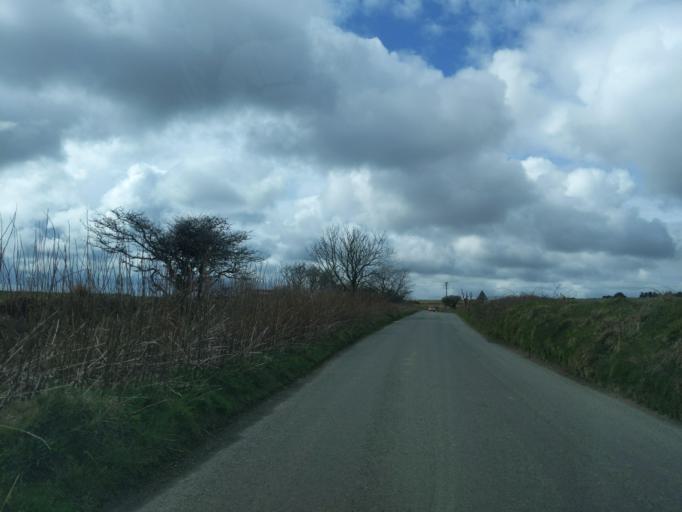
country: GB
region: England
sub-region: Cornwall
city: Camelford
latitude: 50.6406
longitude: -4.6352
